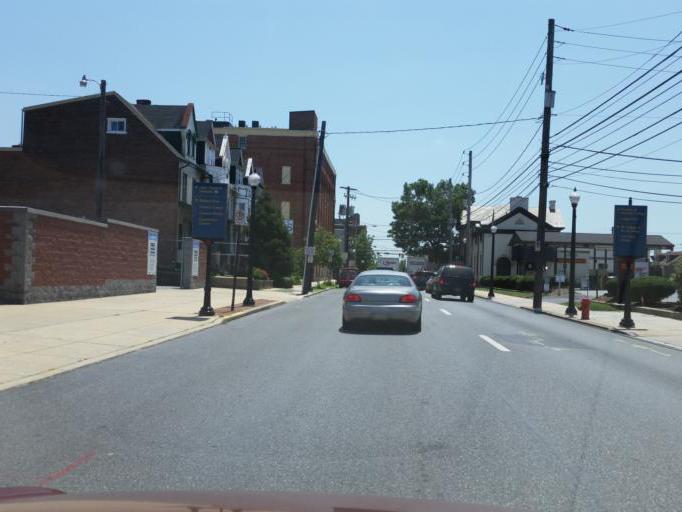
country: US
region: Pennsylvania
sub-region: Lancaster County
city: Lancaster
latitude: 40.0468
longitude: -76.3093
